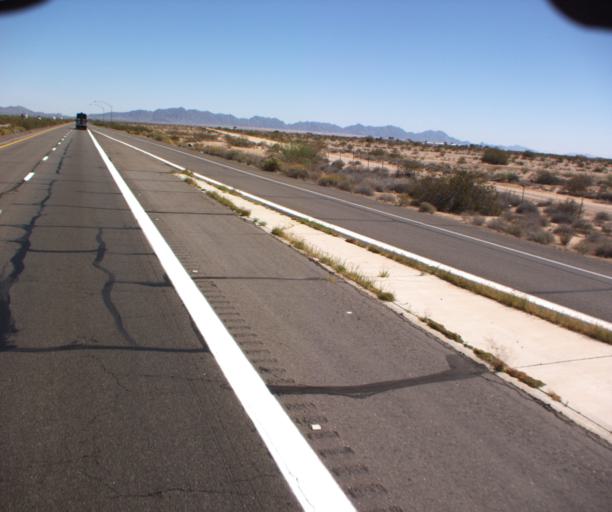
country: US
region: Arizona
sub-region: Yuma County
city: Wellton
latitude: 32.6938
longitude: -113.9501
